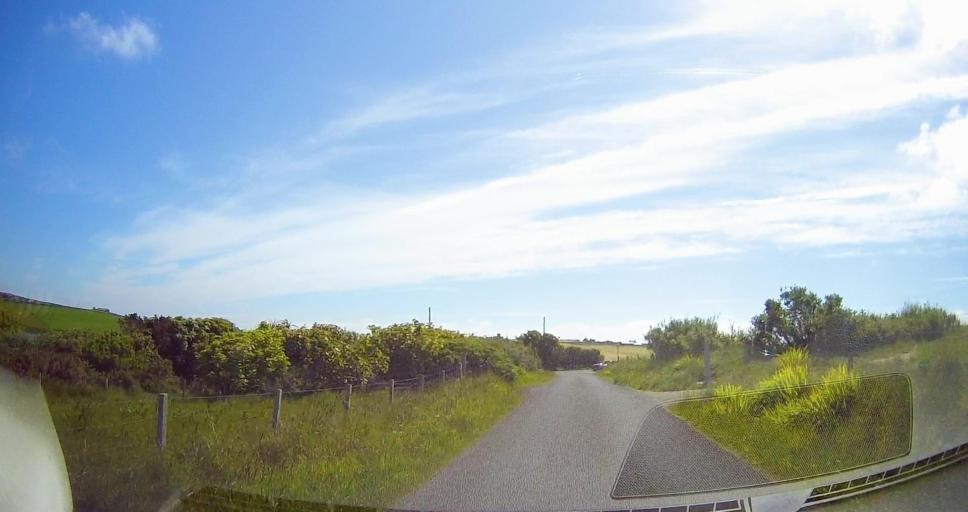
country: GB
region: Scotland
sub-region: Orkney Islands
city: Kirkwall
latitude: 58.8535
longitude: -2.9178
